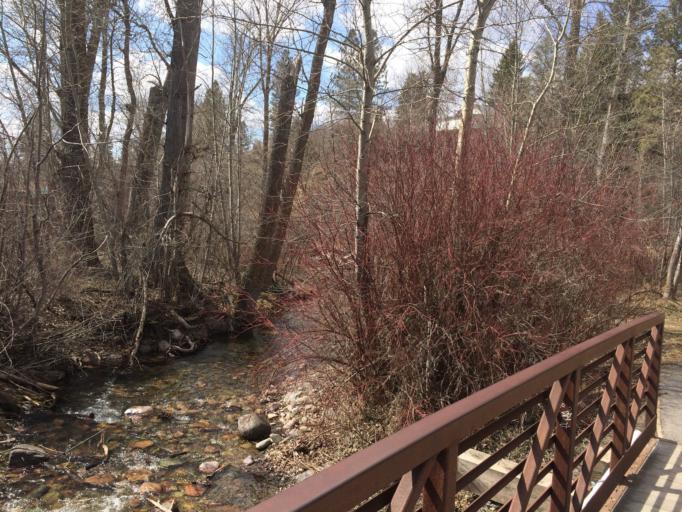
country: US
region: Montana
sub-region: Missoula County
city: Missoula
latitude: 46.8747
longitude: -113.9803
